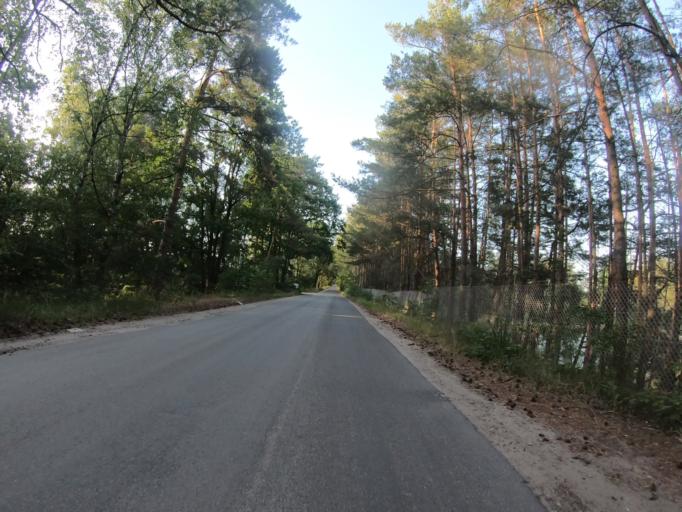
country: DE
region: Lower Saxony
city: Wagenhoff
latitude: 52.5247
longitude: 10.4808
